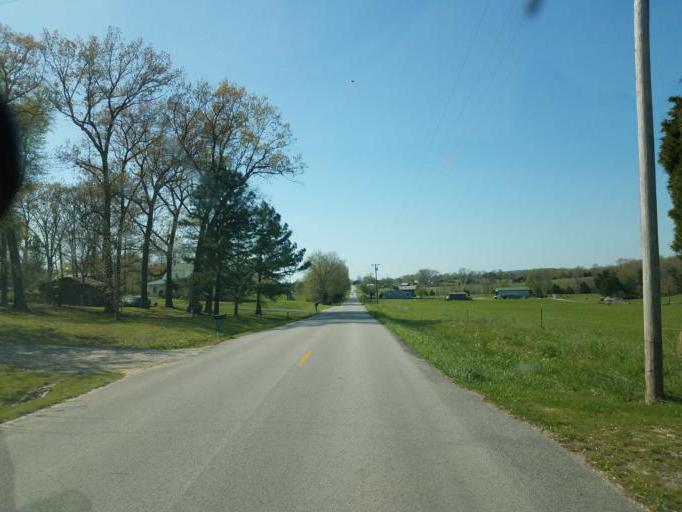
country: US
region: Kentucky
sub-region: Edmonson County
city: Brownsville
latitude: 37.1254
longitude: -86.1579
